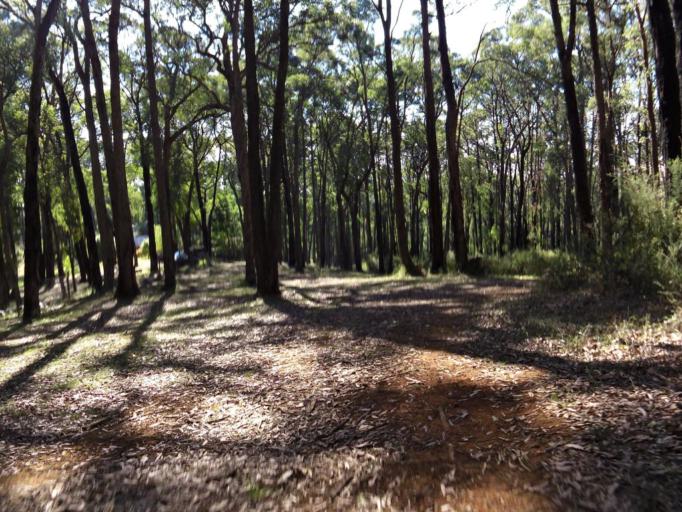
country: AU
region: Victoria
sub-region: Cardinia
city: Cockatoo
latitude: -37.9321
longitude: 145.4677
